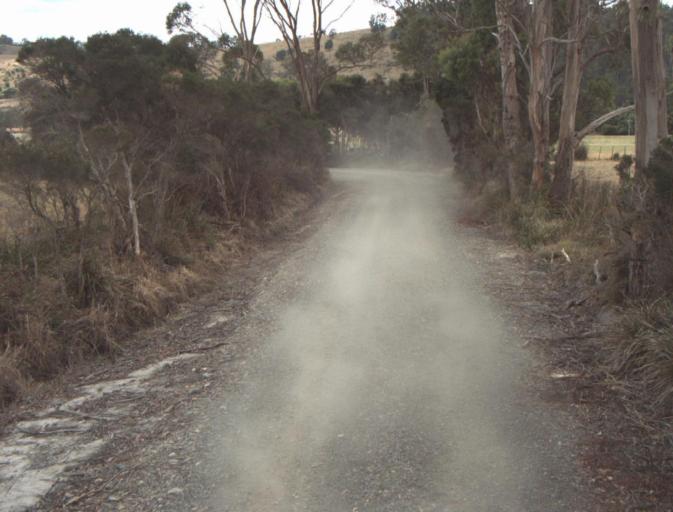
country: AU
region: Tasmania
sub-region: Launceston
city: Mayfield
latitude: -41.2417
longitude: 147.1650
